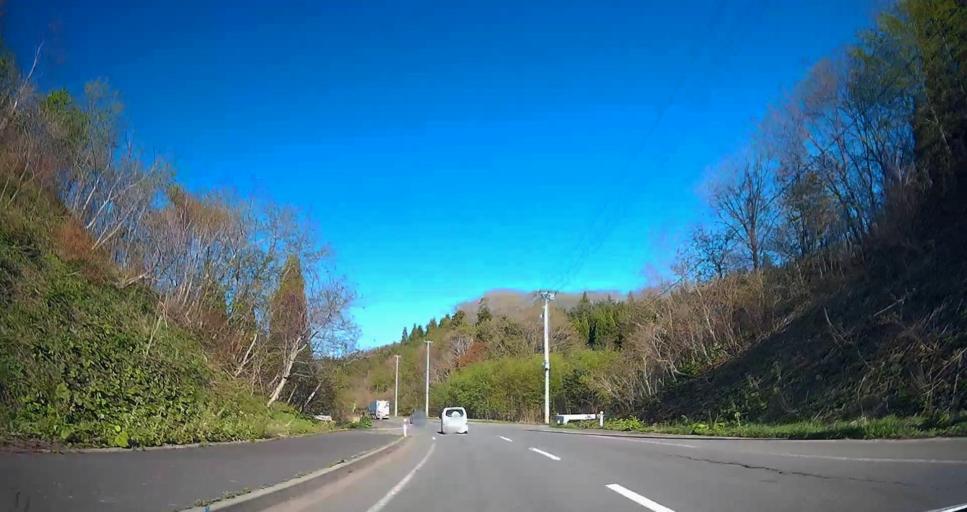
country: JP
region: Aomori
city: Mutsu
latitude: 41.4301
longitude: 141.1397
